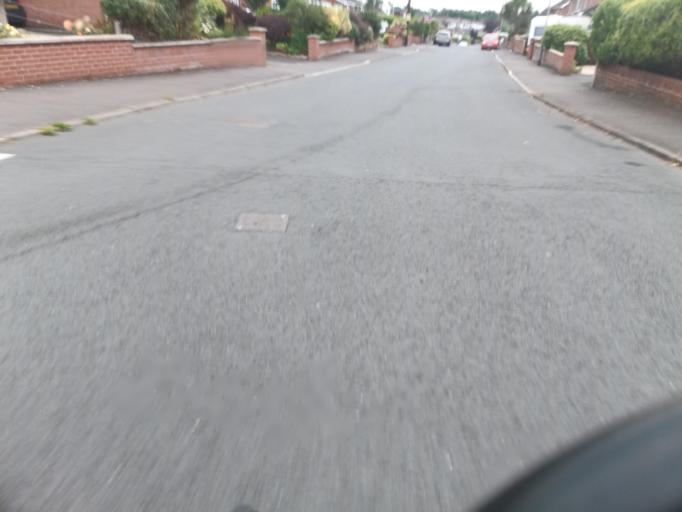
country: GB
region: Northern Ireland
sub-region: Ards District
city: Comber
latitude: 54.5549
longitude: -5.7321
